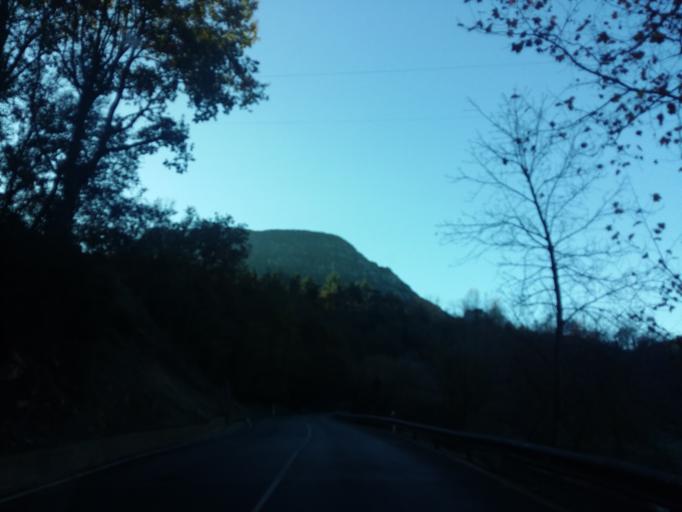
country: ES
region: Cantabria
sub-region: Provincia de Cantabria
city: Ramales de la Victoria
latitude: 43.2465
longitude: -3.4605
